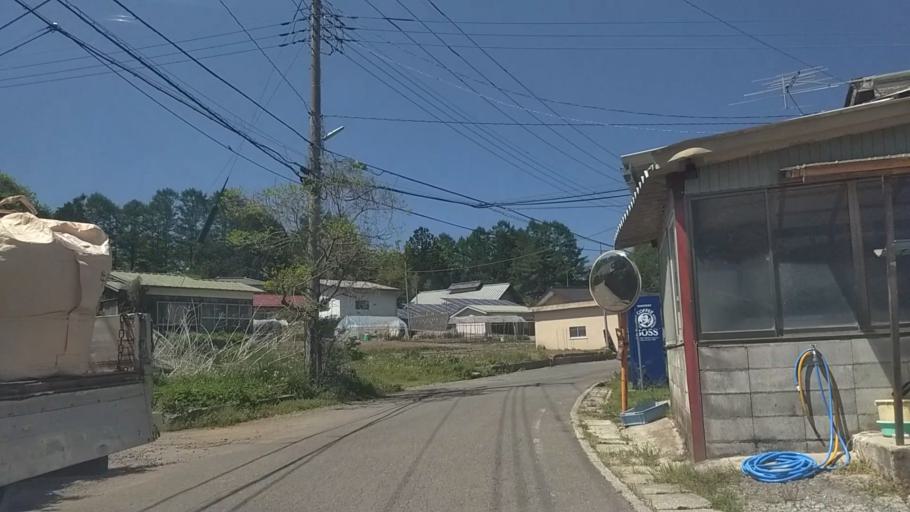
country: JP
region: Yamanashi
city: Nirasaki
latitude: 35.8740
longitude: 138.4529
